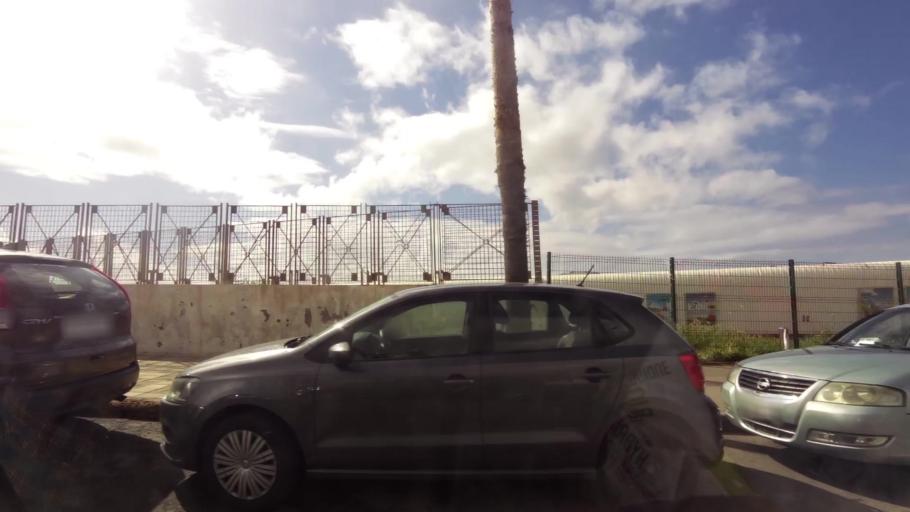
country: MA
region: Grand Casablanca
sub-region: Casablanca
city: Casablanca
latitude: 33.5740
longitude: -7.7066
